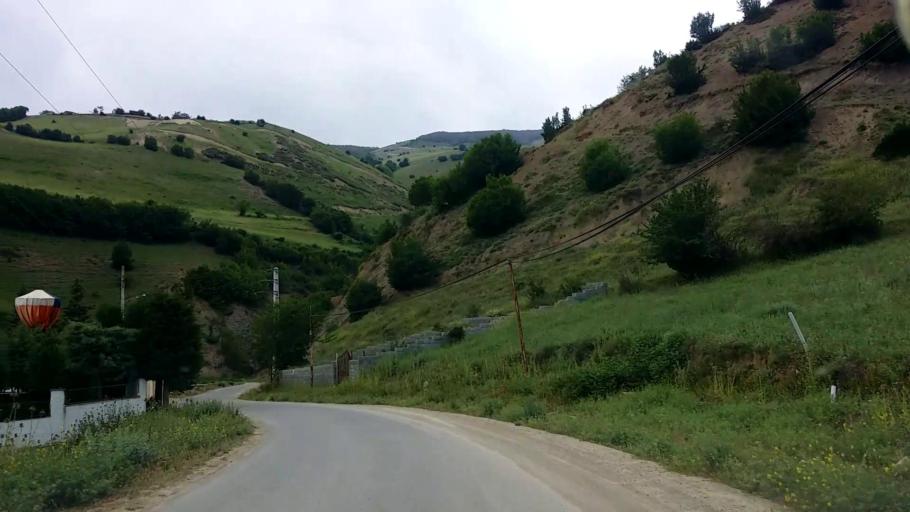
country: IR
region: Mazandaran
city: Chalus
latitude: 36.5533
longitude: 51.2702
